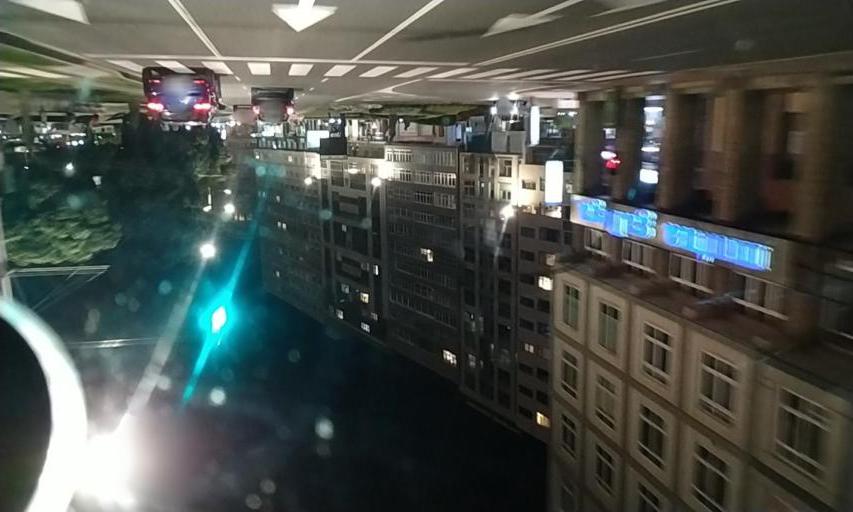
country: ES
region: Galicia
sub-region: Provincia da Coruna
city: A Coruna
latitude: 43.3685
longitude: -8.4103
